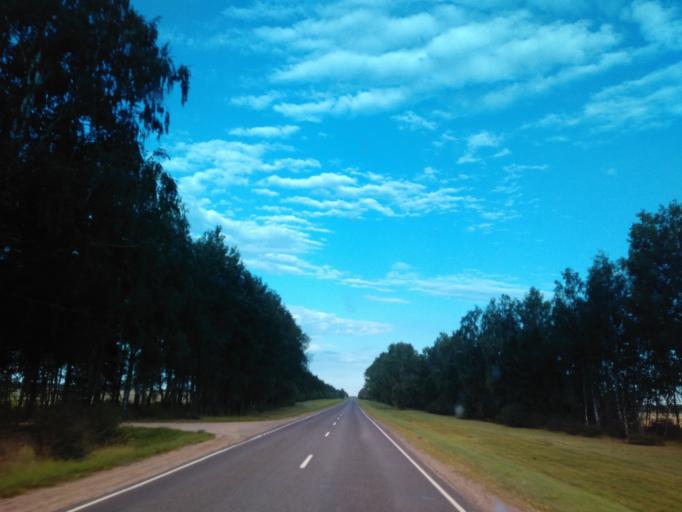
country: BY
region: Minsk
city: Uzda
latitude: 53.4391
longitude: 27.3060
